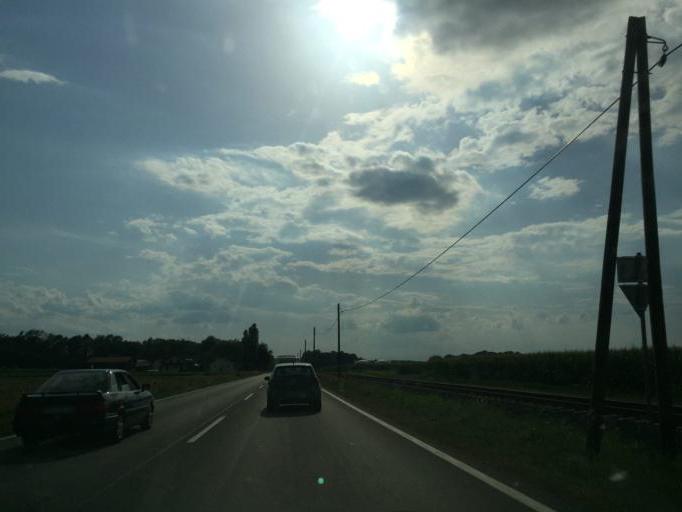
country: AT
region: Styria
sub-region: Politischer Bezirk Suedoststeiermark
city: Ratschendorf
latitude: 46.7275
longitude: 15.8191
